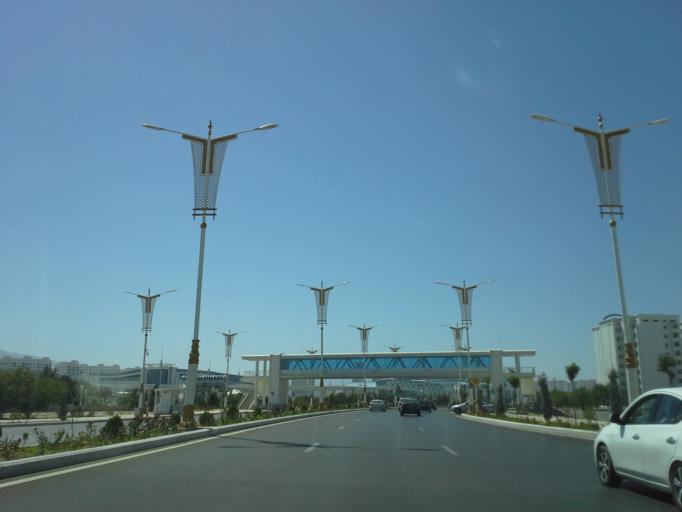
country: TM
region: Ahal
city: Ashgabat
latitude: 37.9106
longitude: 58.3863
